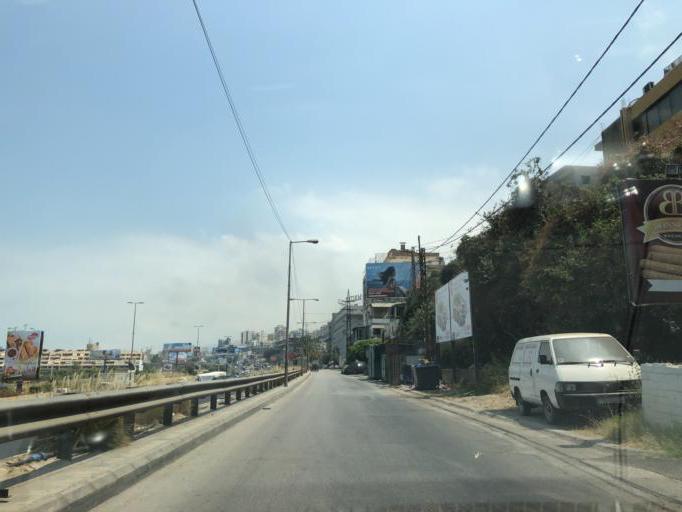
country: LB
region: Mont-Liban
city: Djounie
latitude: 33.9580
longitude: 35.6015
